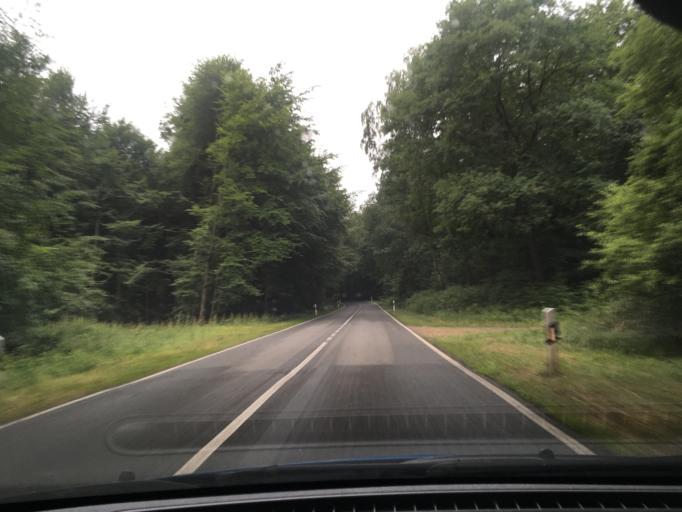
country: DE
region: Lower Saxony
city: Egestorf
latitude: 53.2143
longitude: 10.0759
